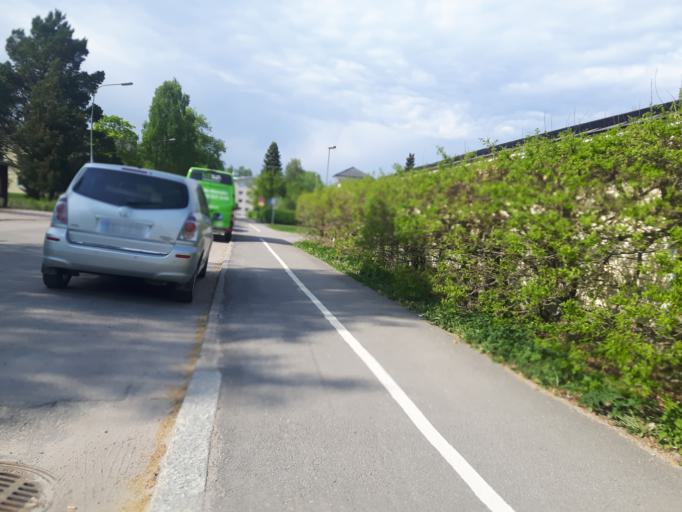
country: FI
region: Uusimaa
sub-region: Porvoo
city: Porvoo
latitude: 60.3939
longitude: 25.6717
